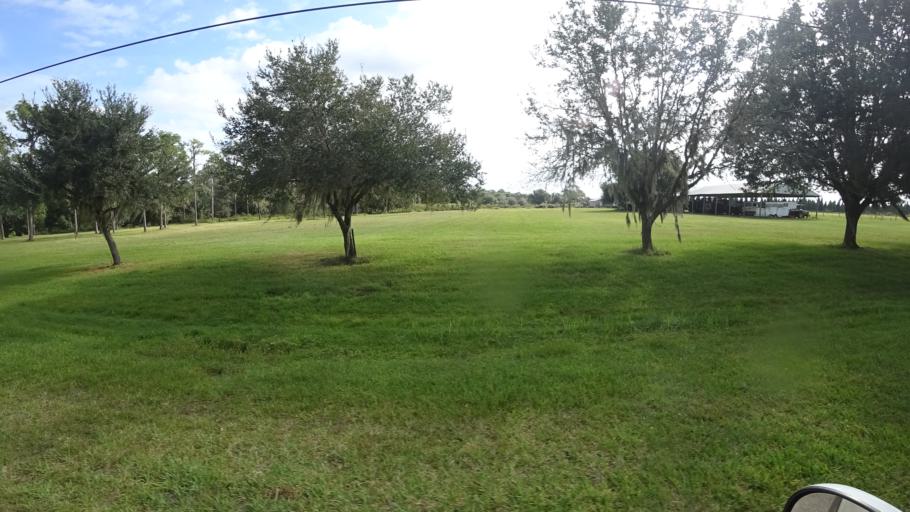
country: US
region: Florida
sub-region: Hillsborough County
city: Wimauma
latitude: 27.5922
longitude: -82.3379
